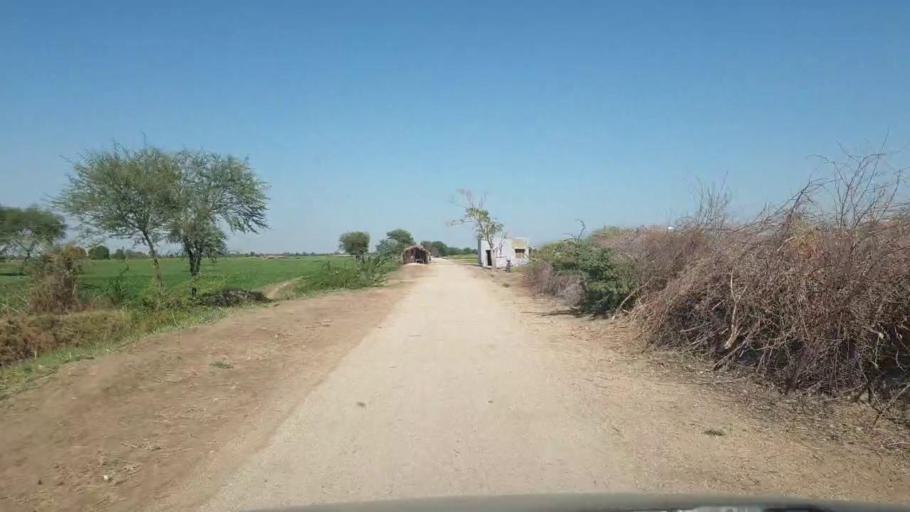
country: PK
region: Sindh
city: Dhoro Naro
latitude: 25.3792
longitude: 69.6001
